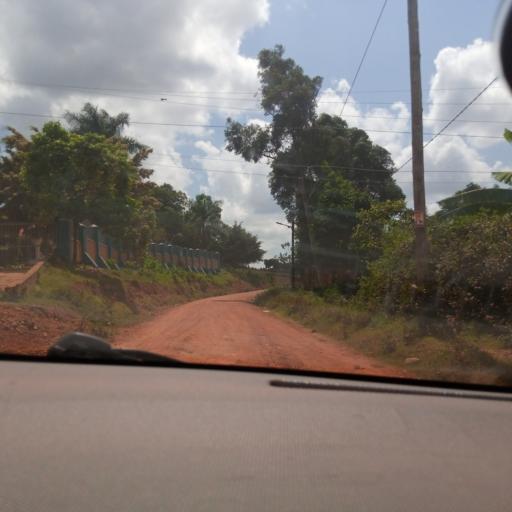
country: UG
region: Central Region
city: Masaka
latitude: -0.3256
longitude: 31.7410
